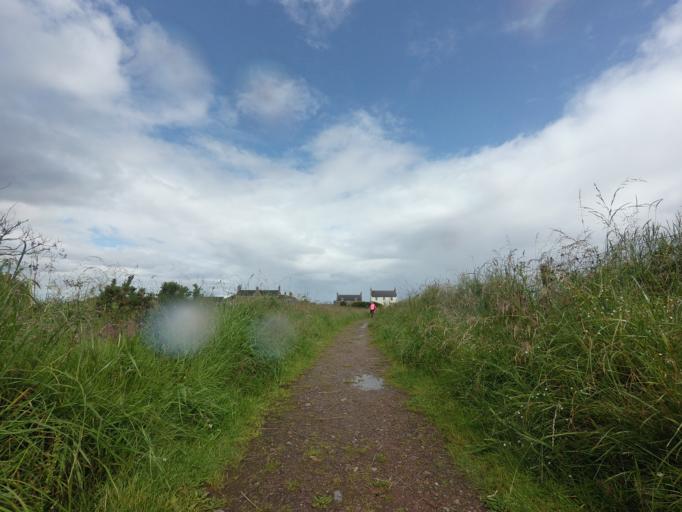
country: GB
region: Scotland
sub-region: Moray
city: Fochabers
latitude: 57.6719
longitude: -3.0924
